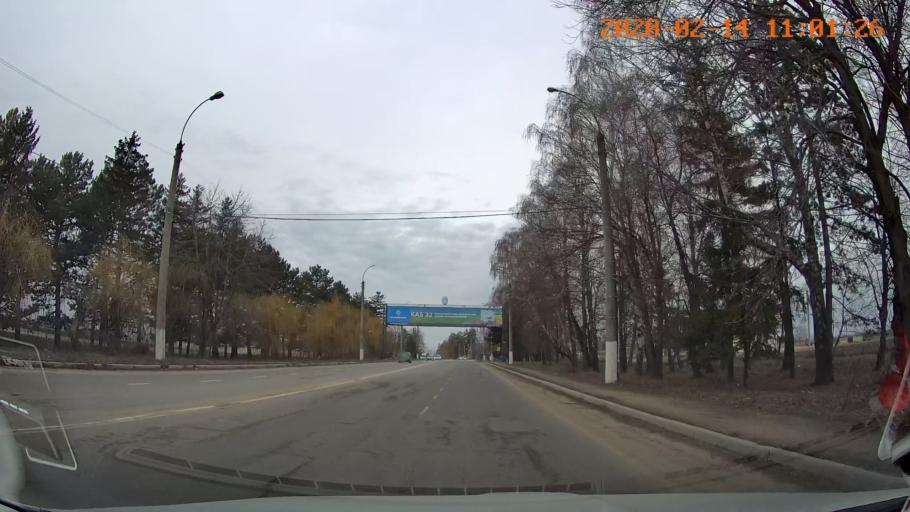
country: MD
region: Raionul Edinet
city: Edinet
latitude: 48.1597
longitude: 27.3291
